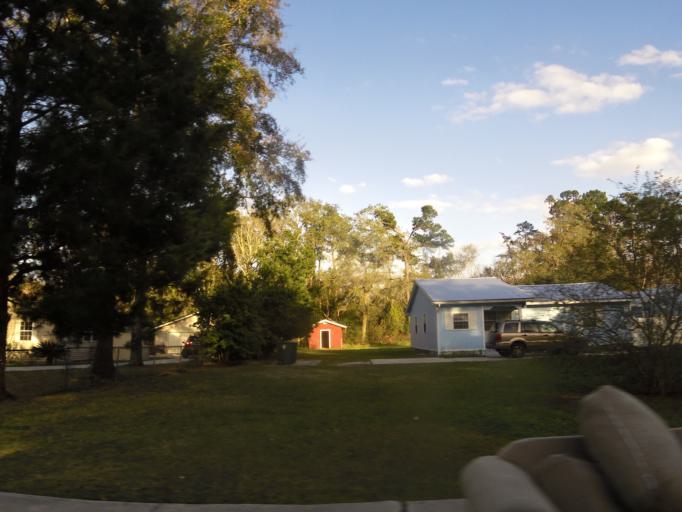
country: US
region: Florida
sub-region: Duval County
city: Jacksonville
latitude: 30.2631
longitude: -81.5798
